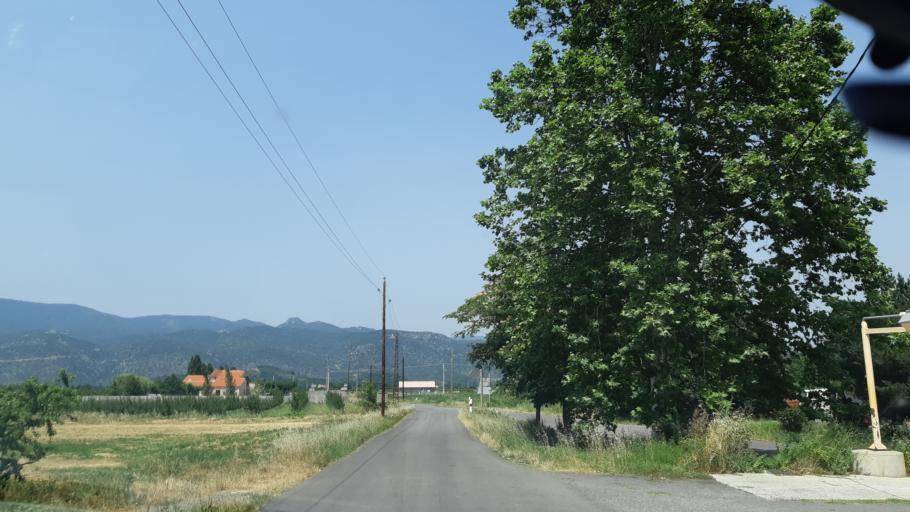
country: FR
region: Languedoc-Roussillon
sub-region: Departement des Pyrenees-Orientales
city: Vinca
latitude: 42.6204
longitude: 2.5187
